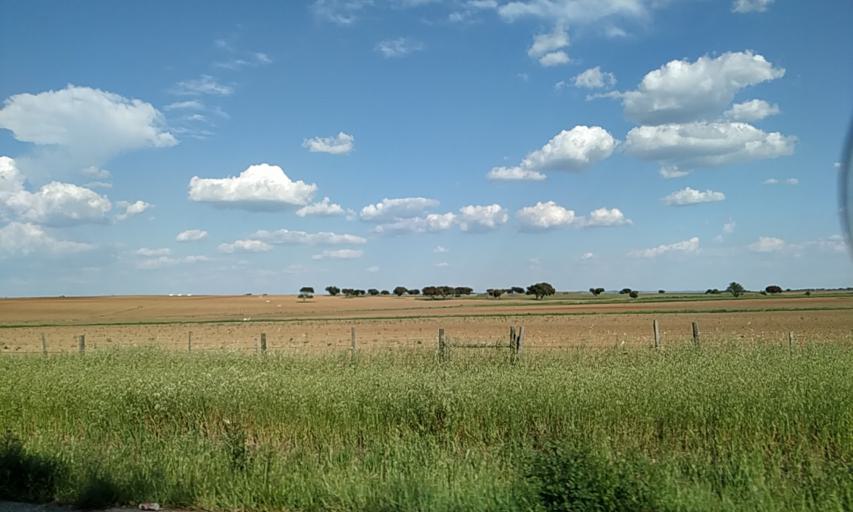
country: PT
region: Evora
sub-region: Estremoz
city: Estremoz
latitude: 38.9782
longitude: -7.4858
